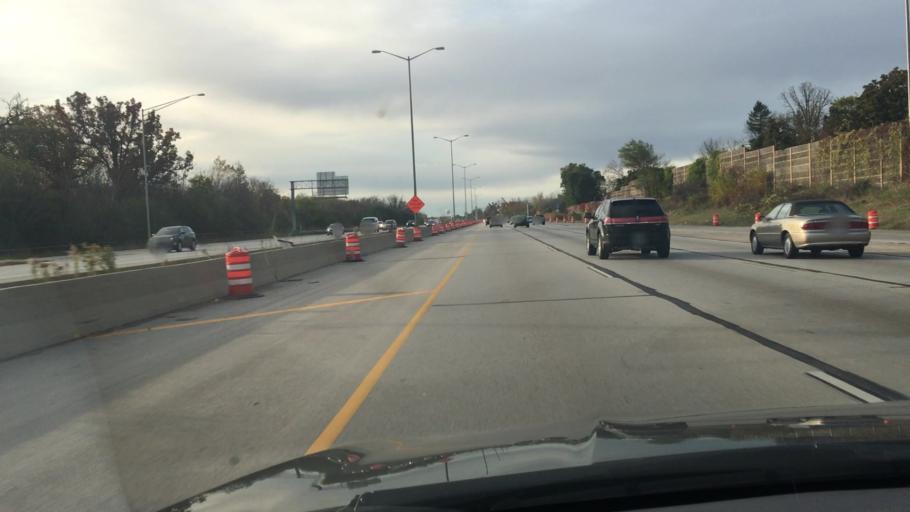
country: US
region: Wisconsin
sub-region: Waukesha County
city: Butler
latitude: 43.1028
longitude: -88.0583
